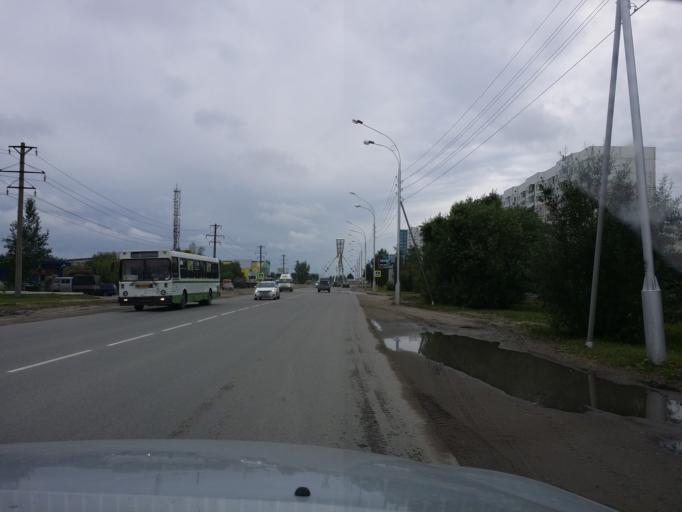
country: RU
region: Khanty-Mansiyskiy Avtonomnyy Okrug
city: Nizhnevartovsk
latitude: 60.9259
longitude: 76.6044
